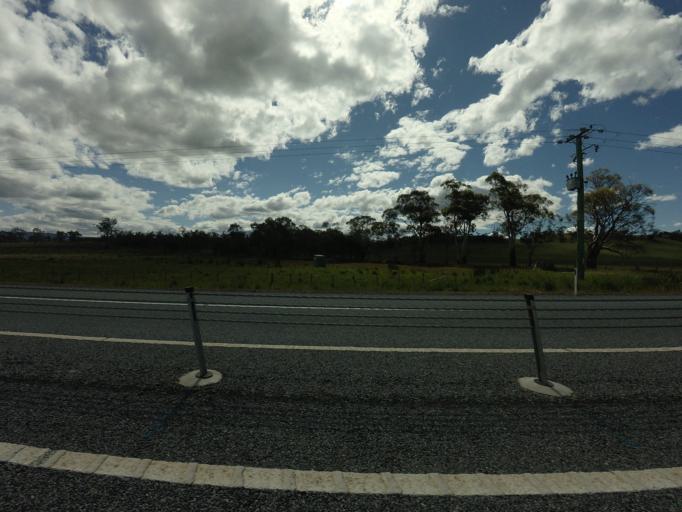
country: AU
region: Tasmania
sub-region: Northern Midlands
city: Evandale
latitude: -42.0736
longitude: 147.4603
